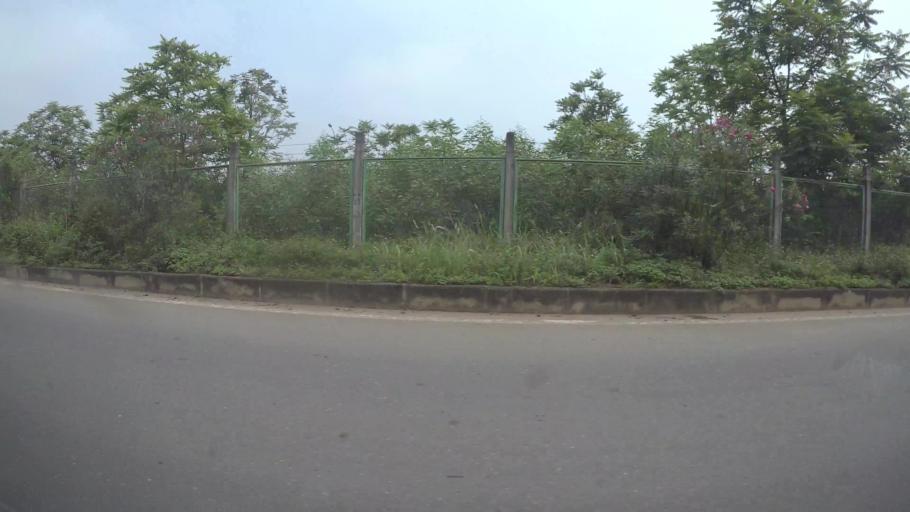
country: VN
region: Ha Noi
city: Lien Quan
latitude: 20.9885
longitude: 105.5713
